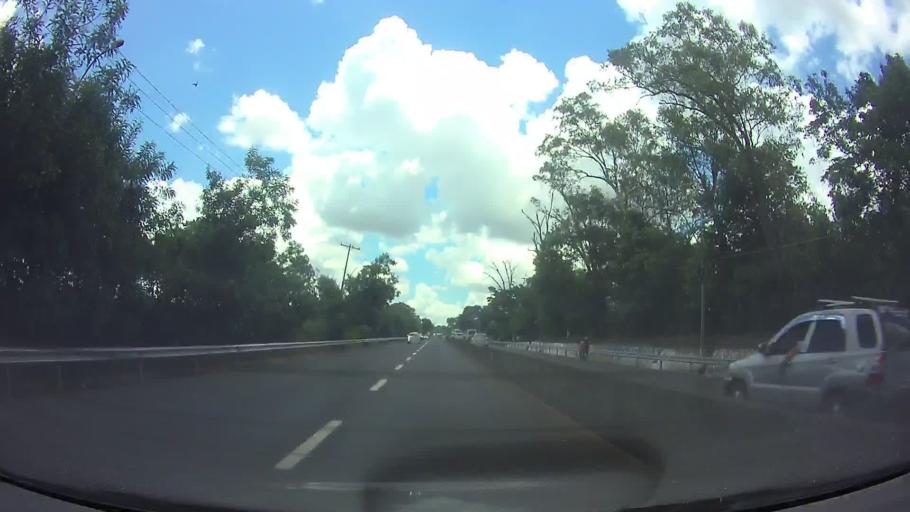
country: PY
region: Central
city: Capiata
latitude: -25.3729
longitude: -57.4119
